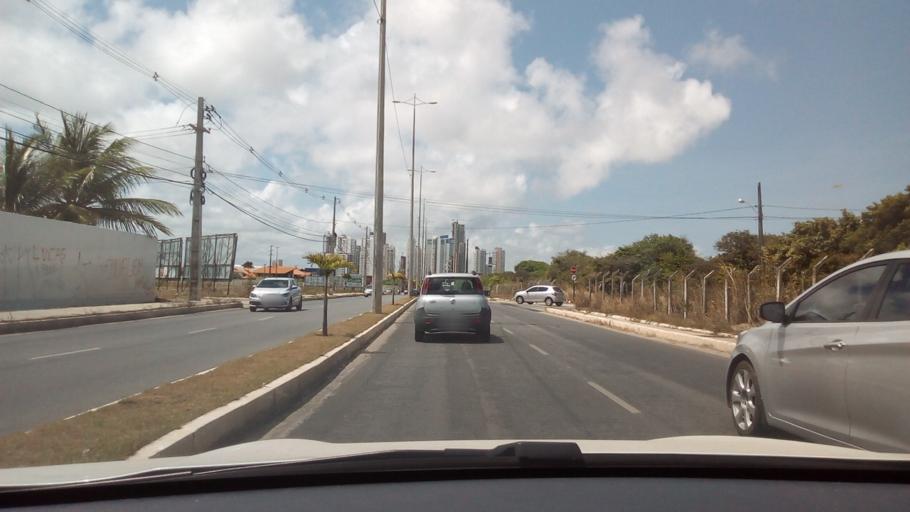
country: BR
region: Paraiba
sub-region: Joao Pessoa
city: Joao Pessoa
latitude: -7.1423
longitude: -34.8170
